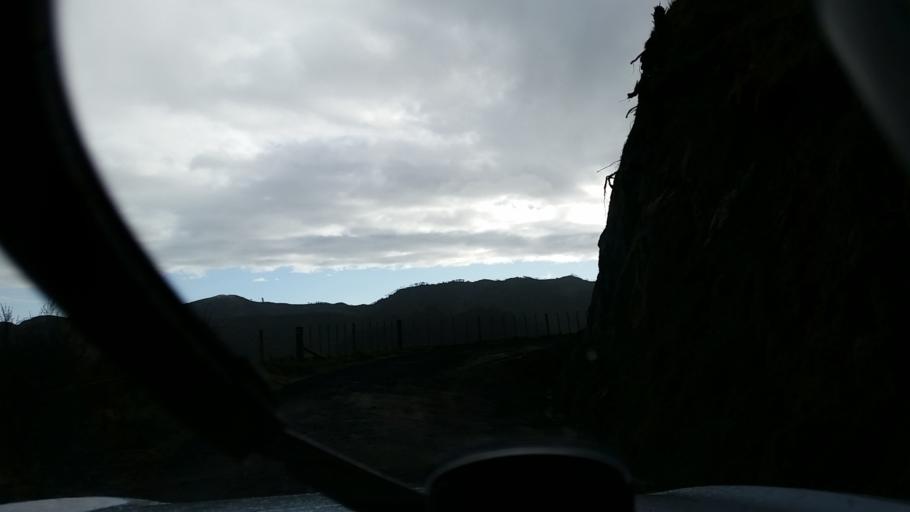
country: NZ
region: Taranaki
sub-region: South Taranaki District
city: Eltham
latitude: -39.4091
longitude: 174.5364
